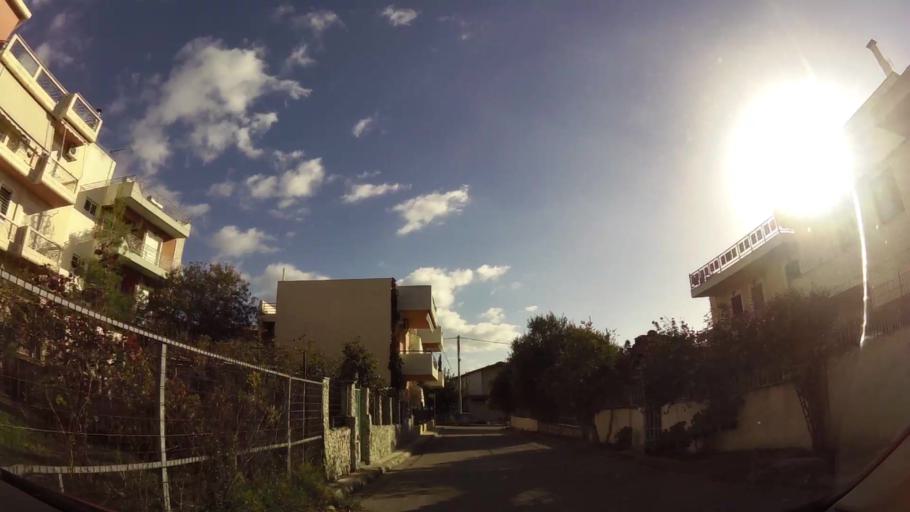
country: GR
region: Attica
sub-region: Nomarchia Anatolikis Attikis
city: Acharnes
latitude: 38.0706
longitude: 23.7423
